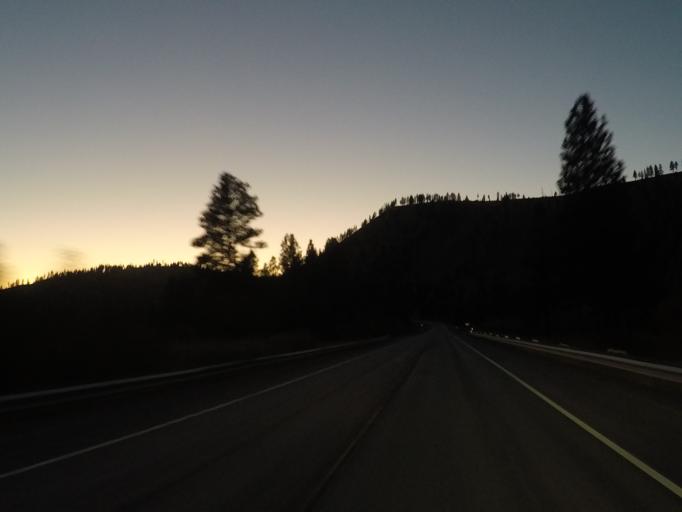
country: US
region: Montana
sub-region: Missoula County
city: Seeley Lake
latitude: 47.0237
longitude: -113.3002
